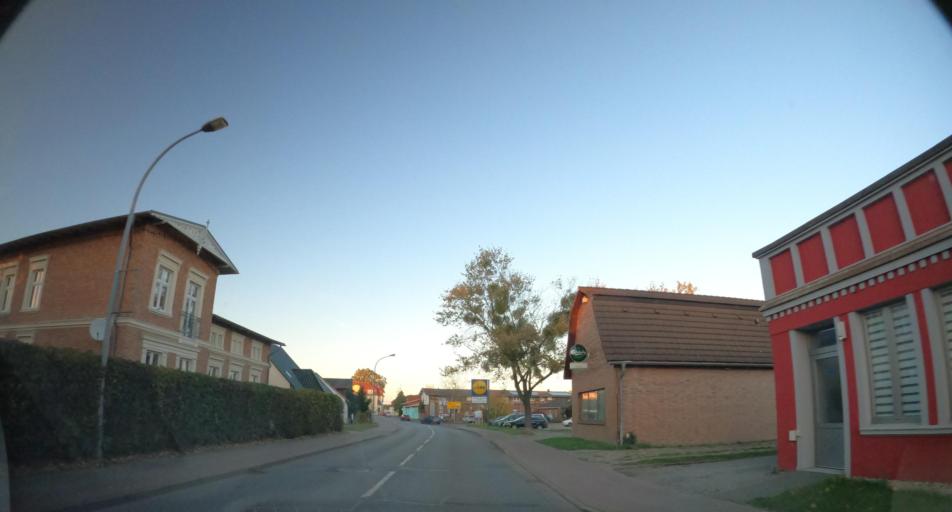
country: DE
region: Mecklenburg-Vorpommern
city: Ueckermunde
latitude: 53.7374
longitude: 14.0405
